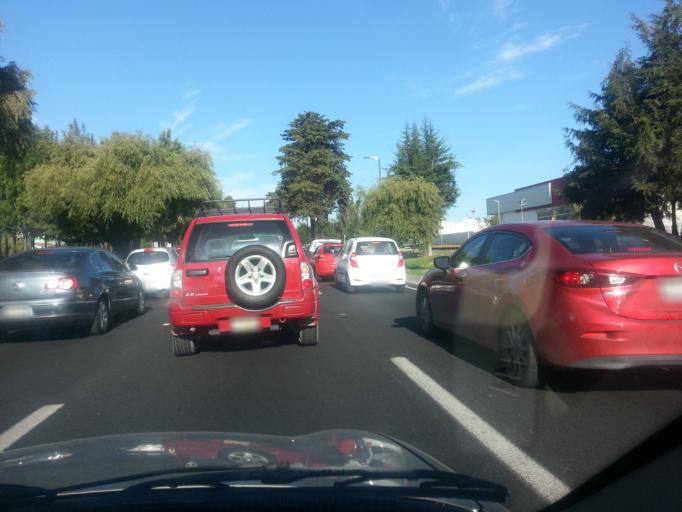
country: MX
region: Mexico
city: Santa Maria Totoltepec
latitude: 19.2880
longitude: -99.6176
